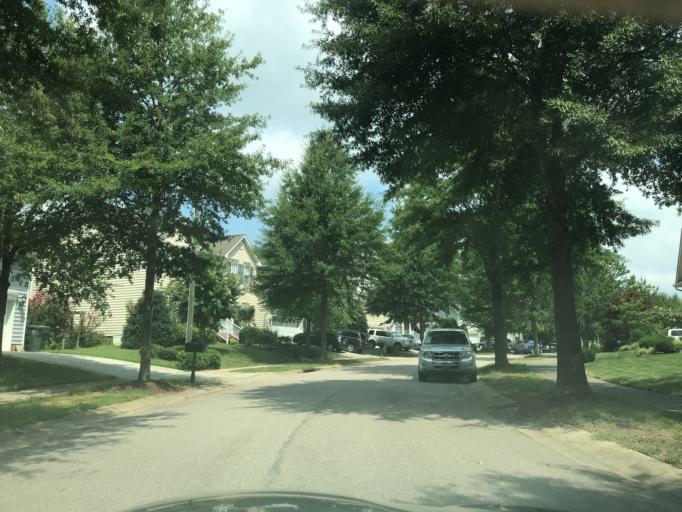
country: US
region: North Carolina
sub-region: Wake County
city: Wake Forest
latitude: 35.9280
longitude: -78.5621
